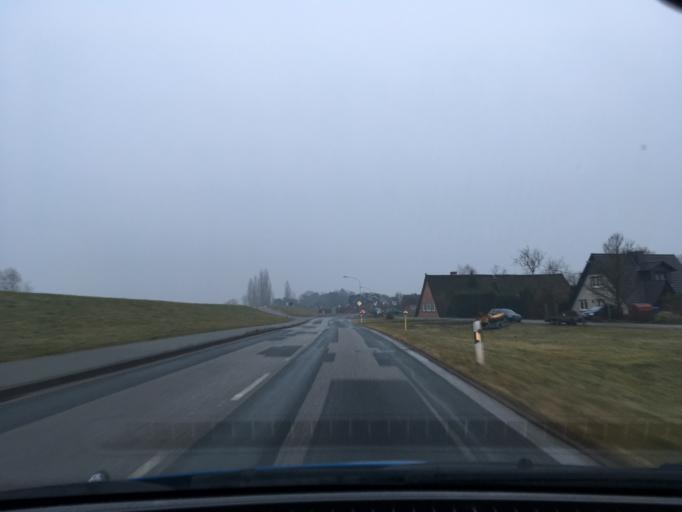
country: DE
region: Hamburg
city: Harburg
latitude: 53.4553
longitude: 10.0641
